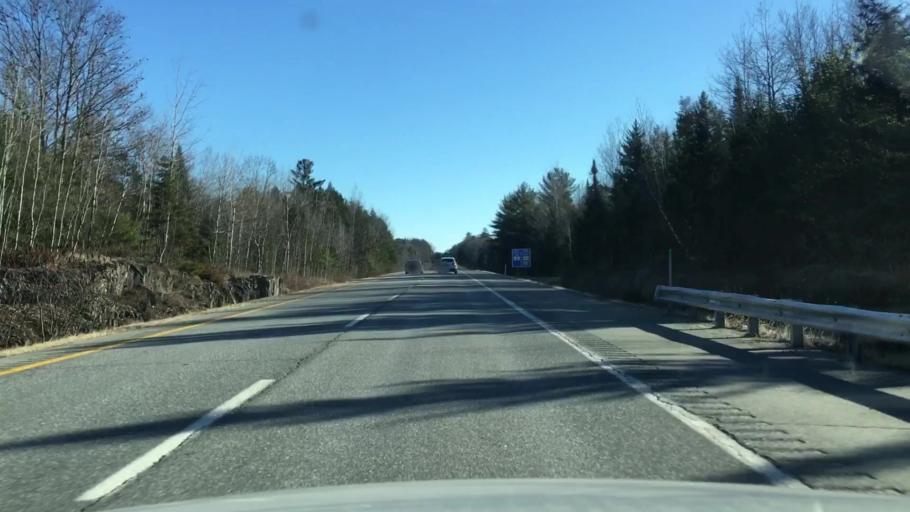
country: US
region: Maine
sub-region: Penobscot County
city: Carmel
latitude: 44.7660
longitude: -68.9939
